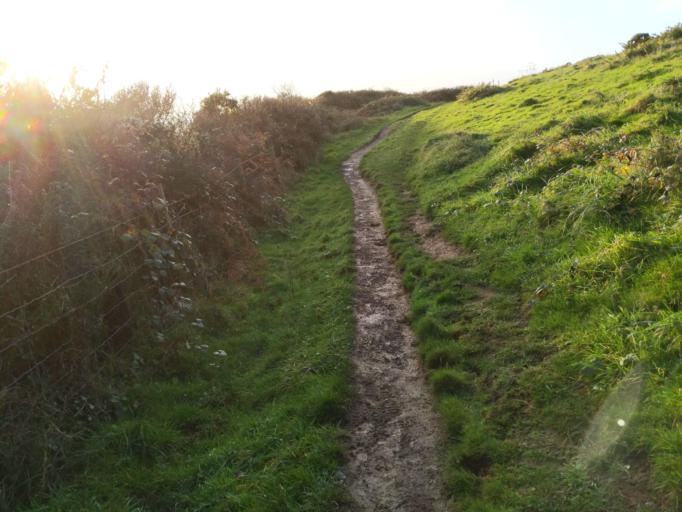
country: GB
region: England
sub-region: Cornwall
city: Fowey
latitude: 50.3248
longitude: -4.6266
